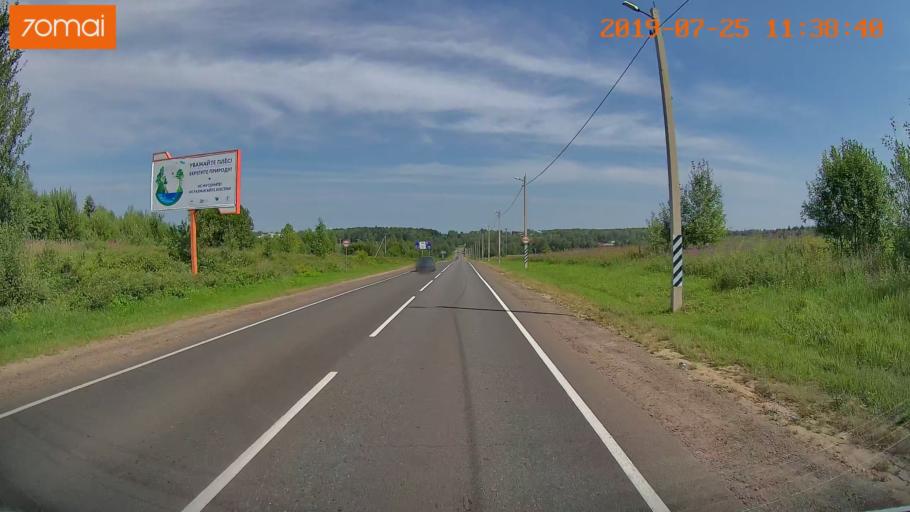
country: RU
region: Ivanovo
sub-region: Privolzhskiy Rayon
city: Ples
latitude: 57.4431
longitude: 41.4863
